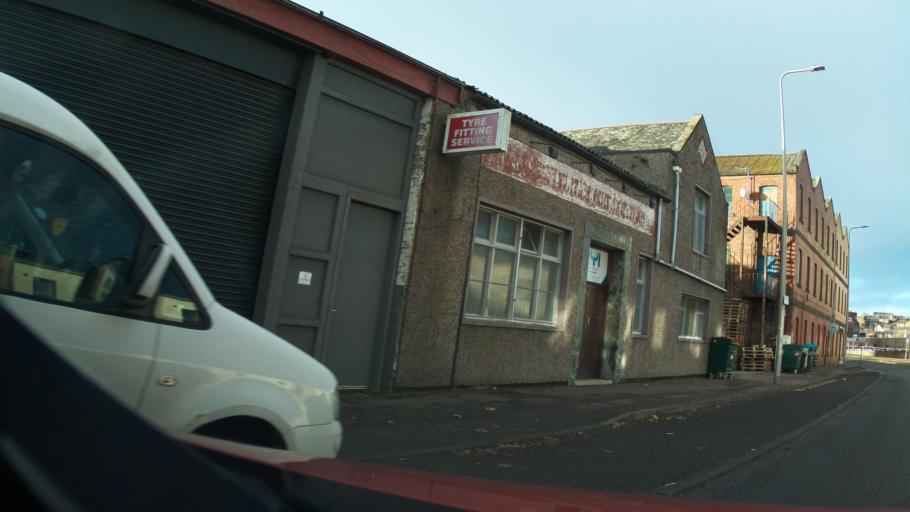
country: GB
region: Scotland
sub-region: Dundee City
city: Dundee
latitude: 56.4591
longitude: -2.9885
